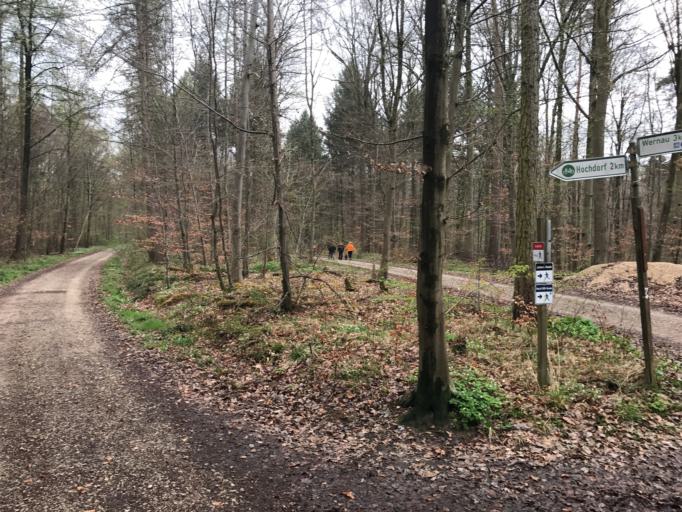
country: DE
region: Baden-Wuerttemberg
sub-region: Regierungsbezirk Stuttgart
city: Notzingen
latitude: 48.6867
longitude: 9.4448
